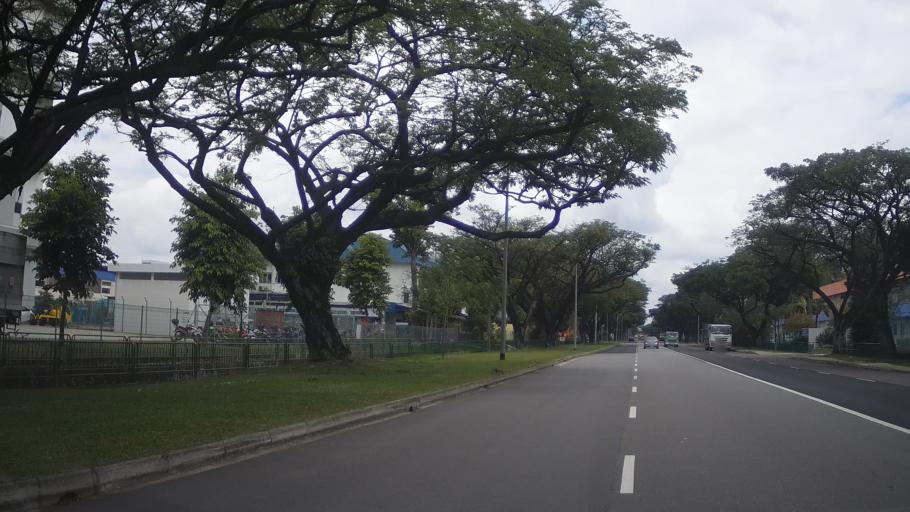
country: MY
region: Johor
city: Johor Bahru
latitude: 1.3132
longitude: 103.6707
